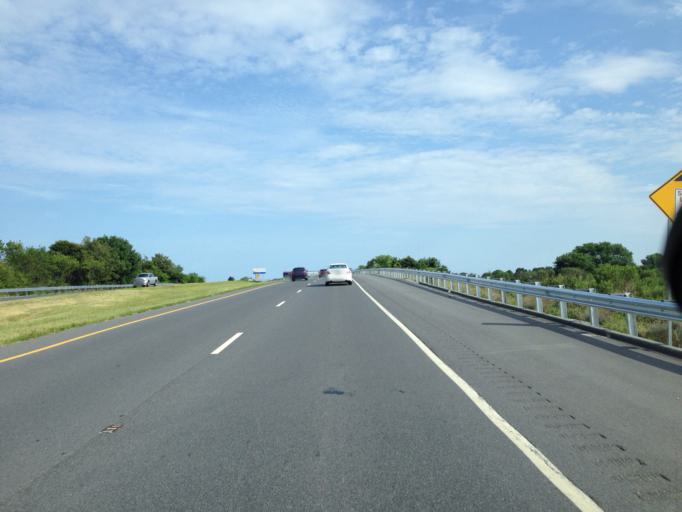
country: US
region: Delaware
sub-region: Sussex County
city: Lewes
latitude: 38.7529
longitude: -75.1909
